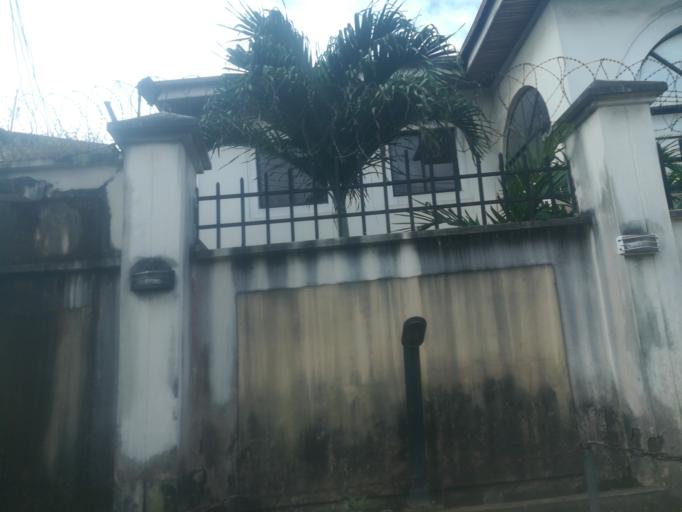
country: NG
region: Lagos
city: Somolu
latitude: 6.5492
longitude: 3.3703
